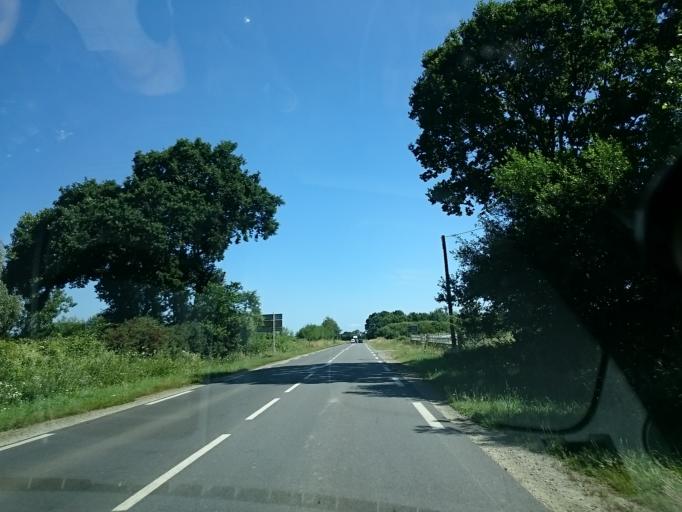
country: FR
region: Brittany
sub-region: Departement d'Ille-et-Vilaine
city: Saint-Pere
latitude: 48.5868
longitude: -1.9076
